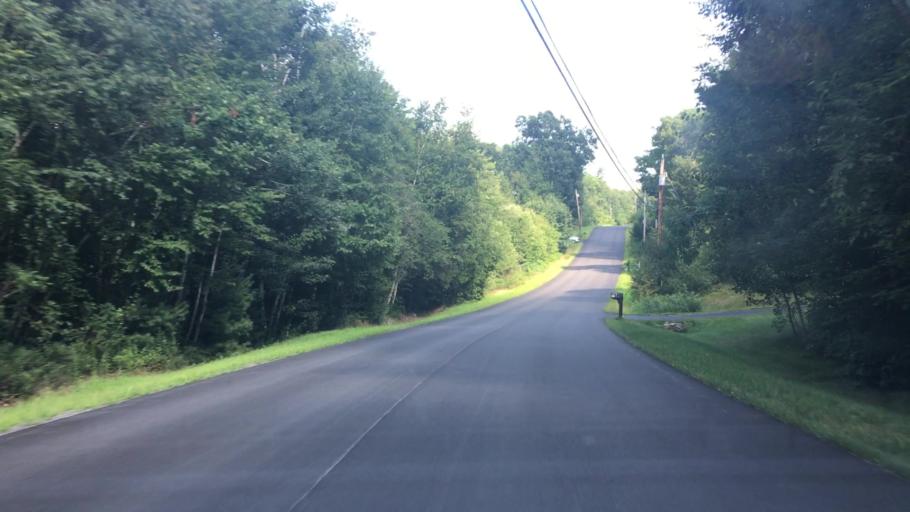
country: US
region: New Hampshire
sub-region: Rockingham County
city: Derry Village
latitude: 42.9390
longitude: -71.3309
